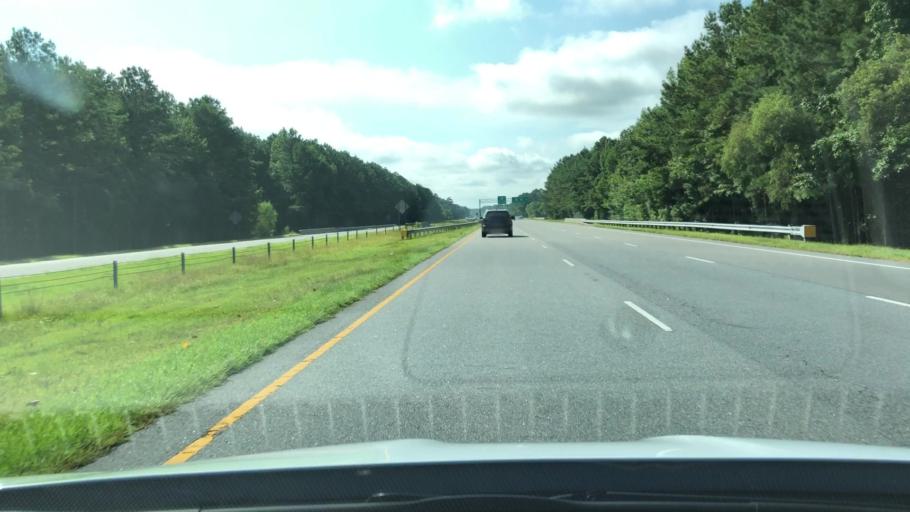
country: US
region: North Carolina
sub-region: Pasquotank County
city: Elizabeth City
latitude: 36.3860
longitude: -76.3173
